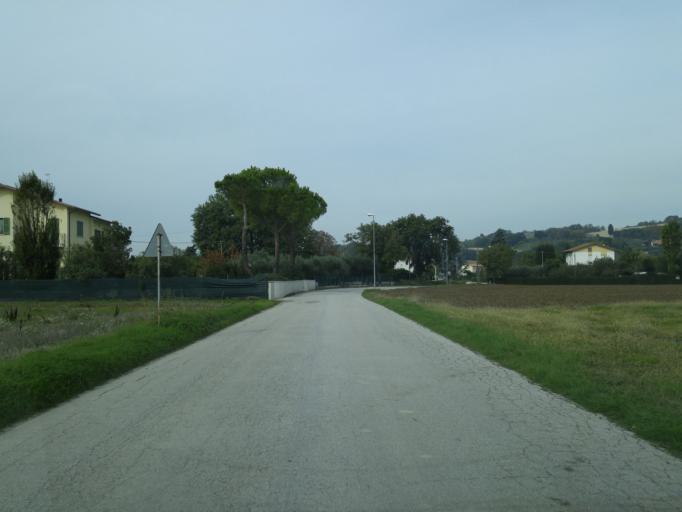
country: IT
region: The Marches
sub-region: Provincia di Pesaro e Urbino
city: Cuccurano
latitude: 43.7915
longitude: 12.9624
